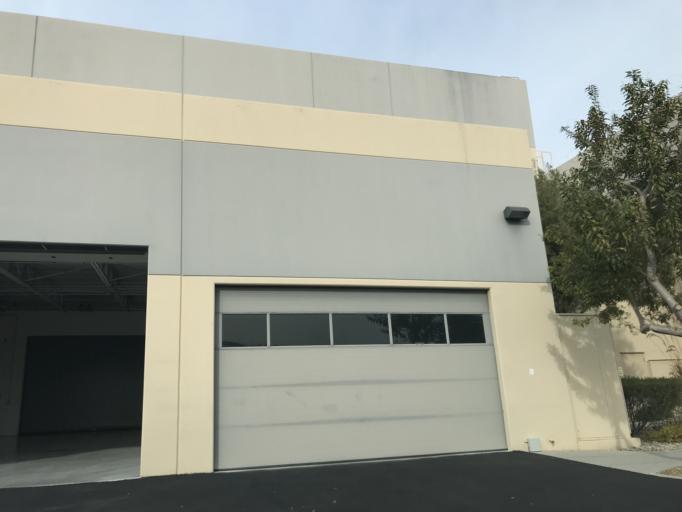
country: US
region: Nevada
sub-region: Clark County
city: Paradise
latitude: 36.0934
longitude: -115.1652
